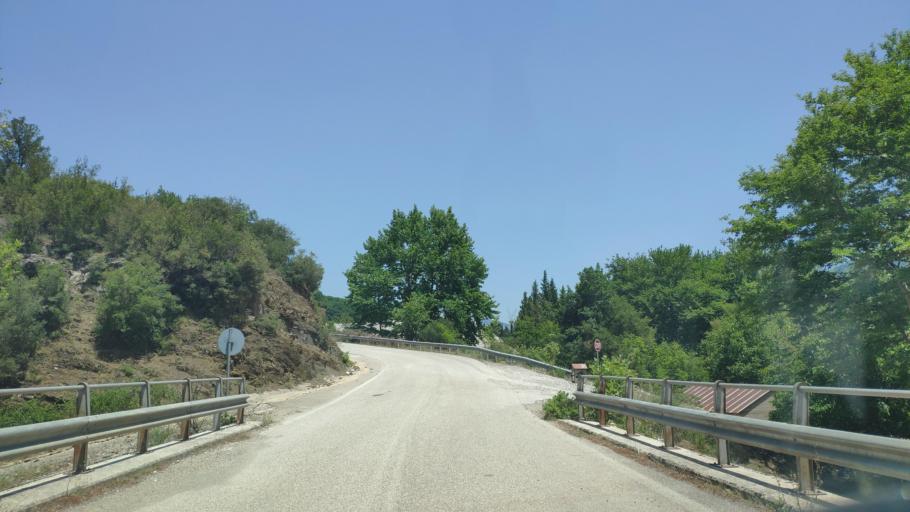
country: GR
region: Epirus
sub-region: Nomos Artas
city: Ano Kalentini
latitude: 39.2117
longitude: 21.3463
